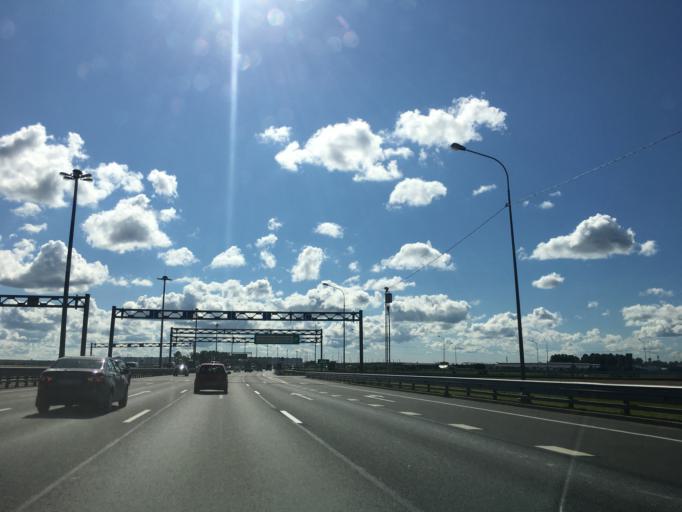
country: RU
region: St.-Petersburg
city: Uritsk
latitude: 59.8158
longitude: 30.2084
